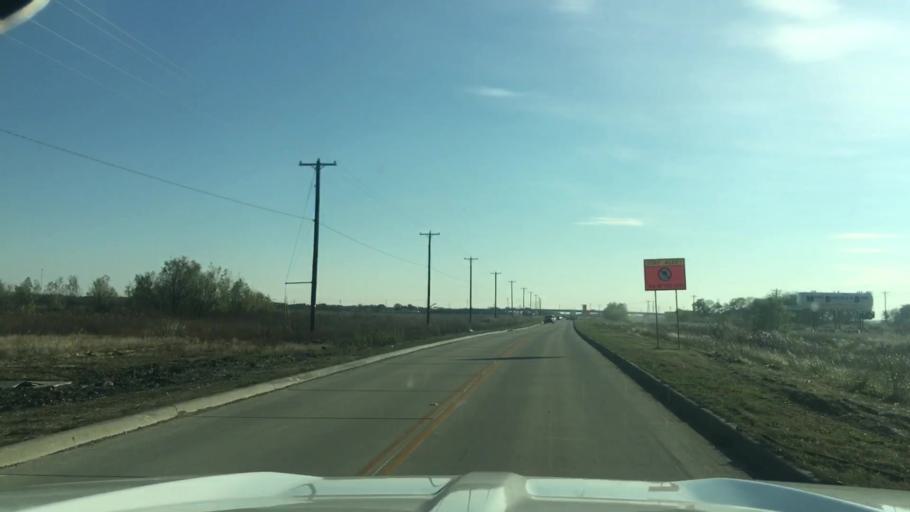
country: US
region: Texas
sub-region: Collin County
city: Prosper
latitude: 33.2284
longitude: -96.8190
